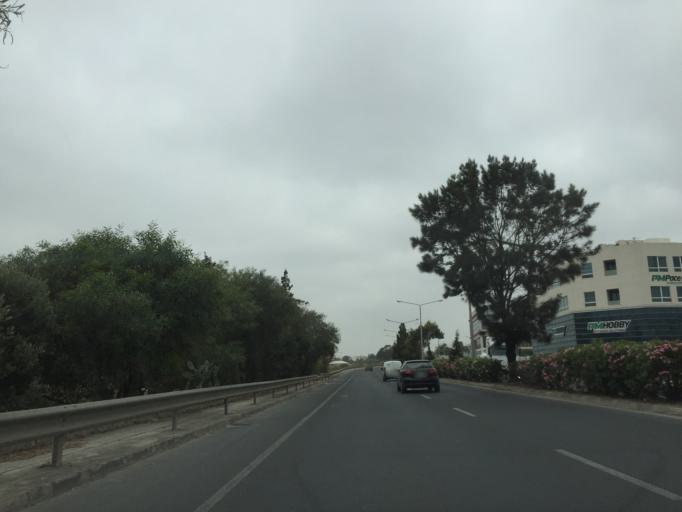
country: MT
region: Birkirkara
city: Birkirkara
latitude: 35.8895
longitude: 14.4607
